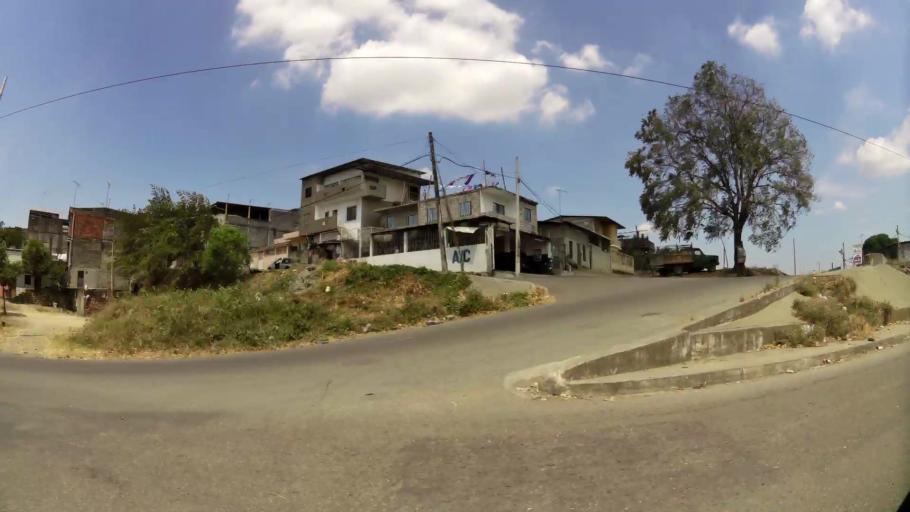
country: EC
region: Guayas
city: Eloy Alfaro
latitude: -2.1157
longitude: -79.9216
